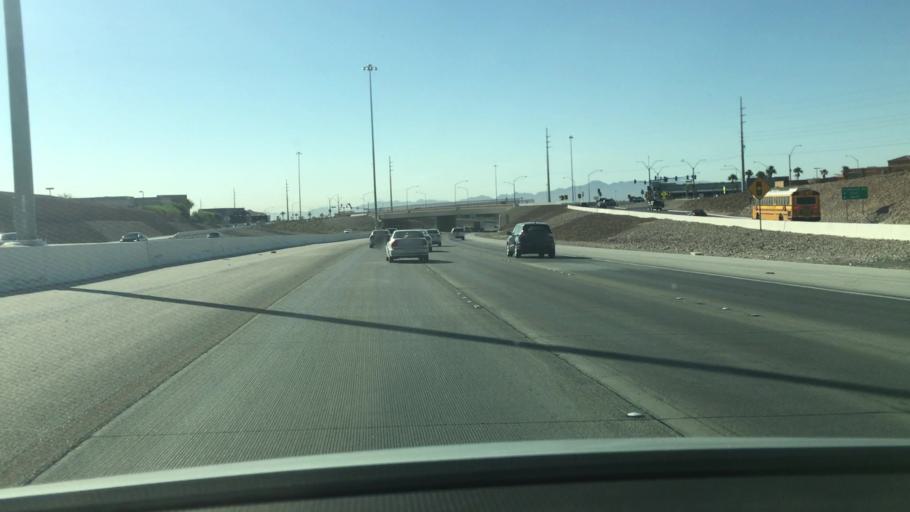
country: US
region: Nevada
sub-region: Clark County
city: Summerlin South
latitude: 36.1169
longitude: -115.3062
